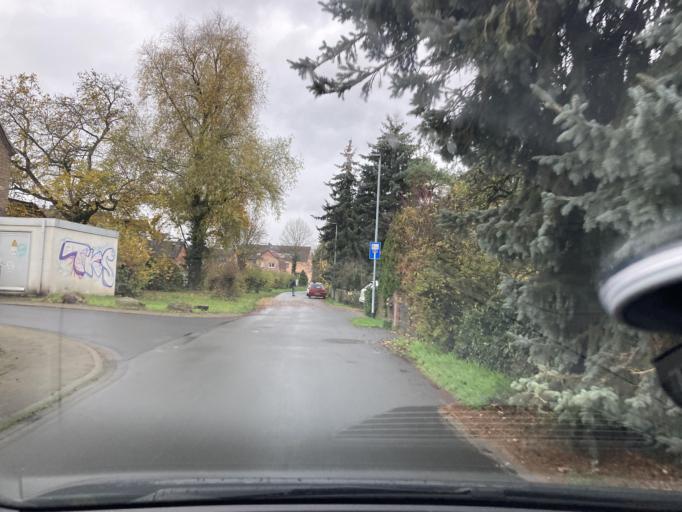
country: DE
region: Hesse
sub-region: Regierungsbezirk Darmstadt
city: Grosskrotzenburg
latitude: 50.0831
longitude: 8.9379
